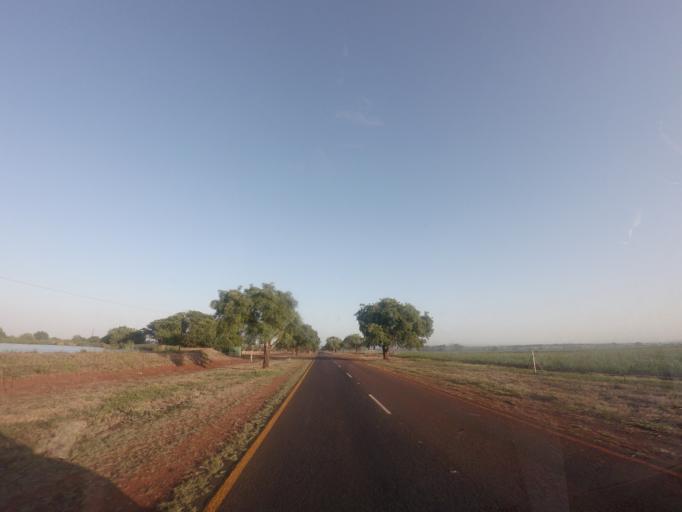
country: ZA
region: Mpumalanga
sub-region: Ehlanzeni District
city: Komatipoort
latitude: -25.3758
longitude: 31.9064
